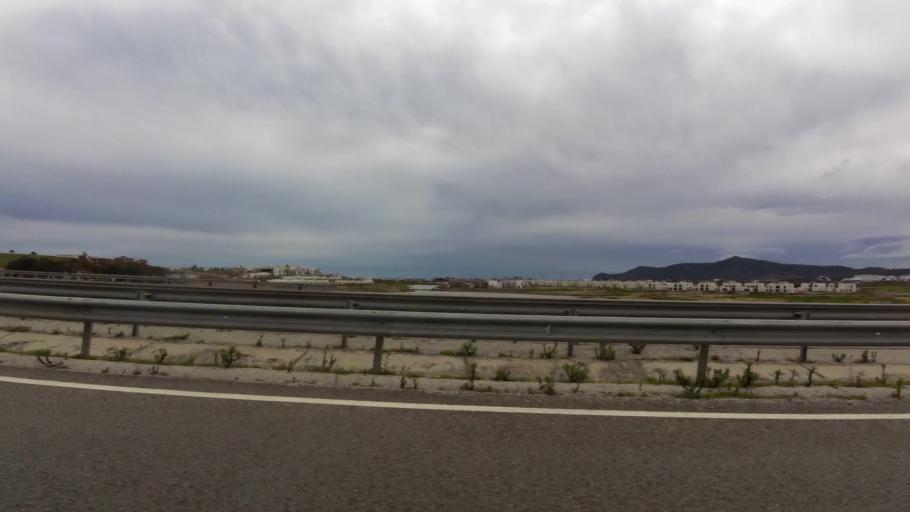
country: MA
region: Tanger-Tetouan
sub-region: Tetouan
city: Martil
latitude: 35.7180
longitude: -5.3539
